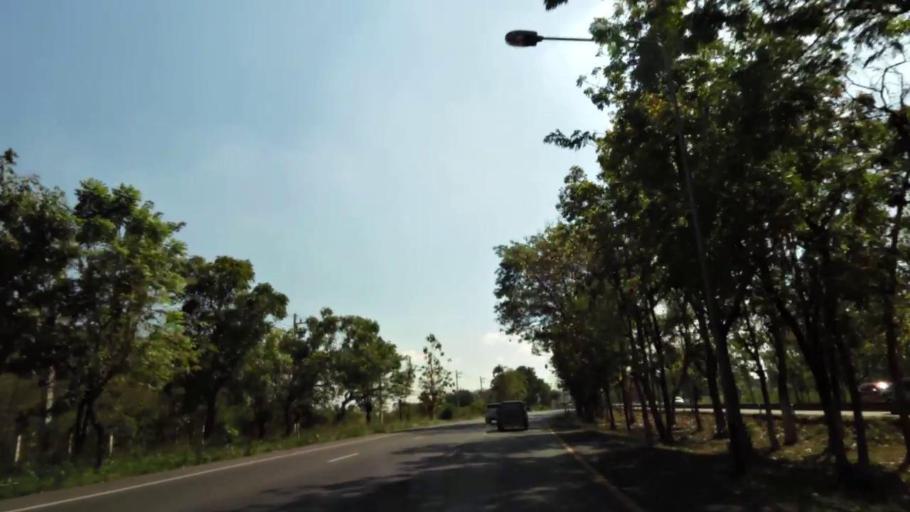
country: TH
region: Nakhon Sawan
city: Nakhon Sawan
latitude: 15.6465
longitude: 100.1348
